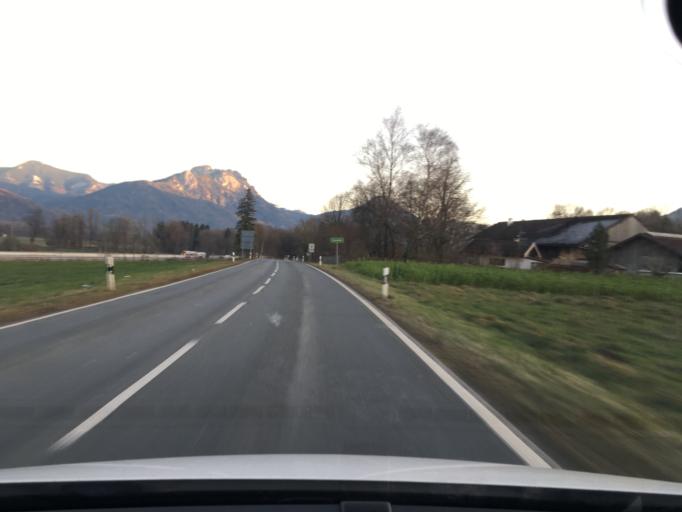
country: DE
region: Bavaria
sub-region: Upper Bavaria
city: Brannenburg
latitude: 47.7582
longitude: 12.1069
